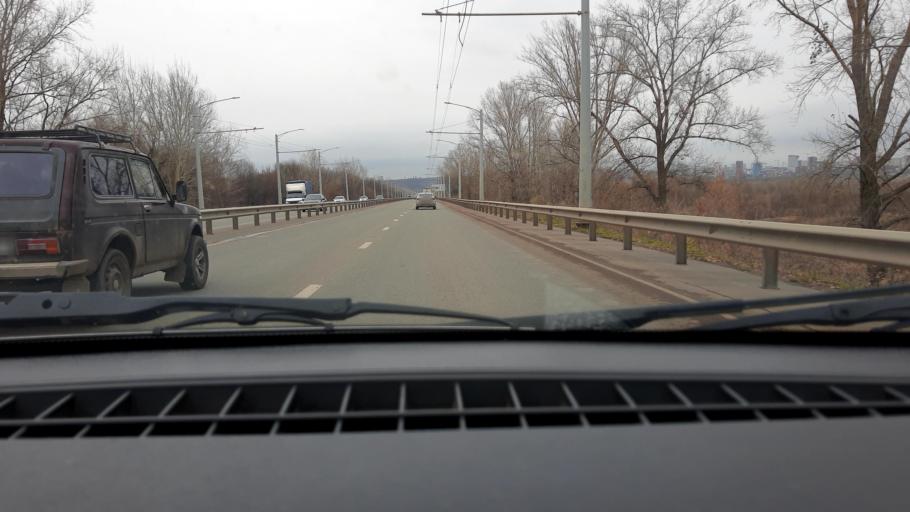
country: RU
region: Bashkortostan
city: Mikhaylovka
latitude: 54.7683
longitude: 55.9213
